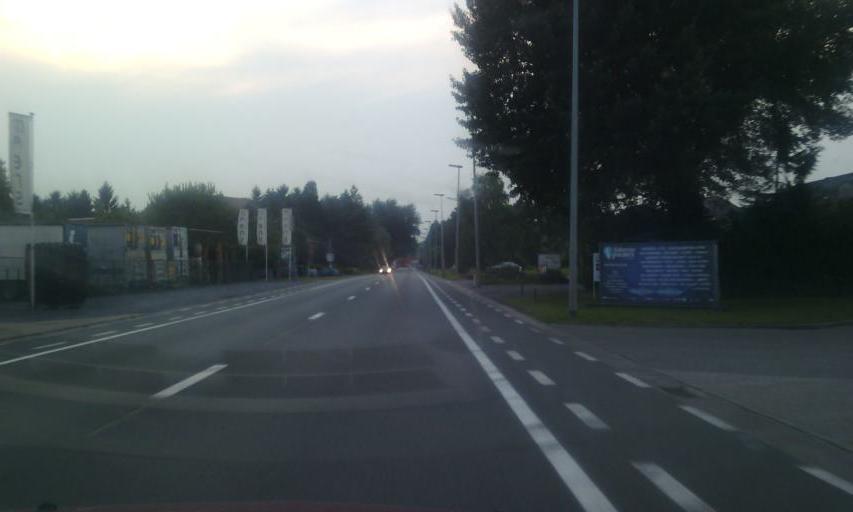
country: BE
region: Flanders
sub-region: Provincie Oost-Vlaanderen
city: Dendermonde
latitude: 51.0426
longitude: 4.0987
